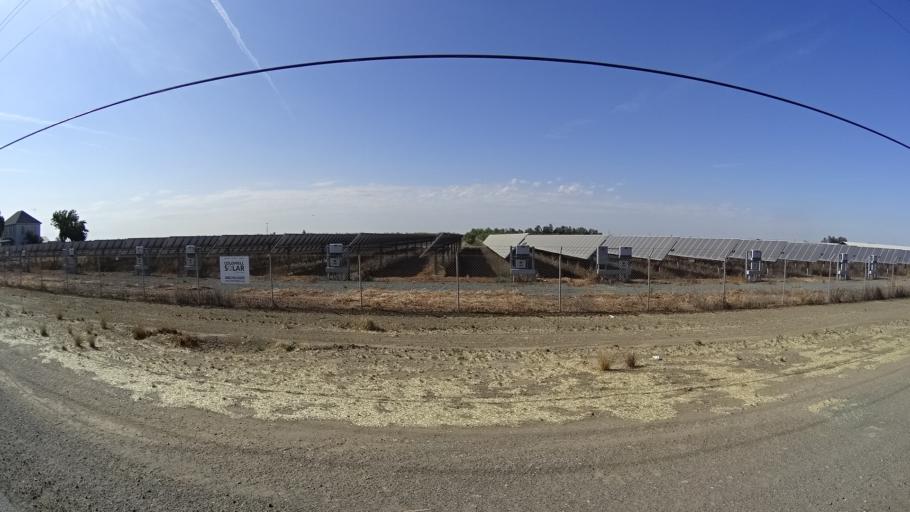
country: US
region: California
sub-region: Kings County
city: Home Garden
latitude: 36.2259
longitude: -119.6187
